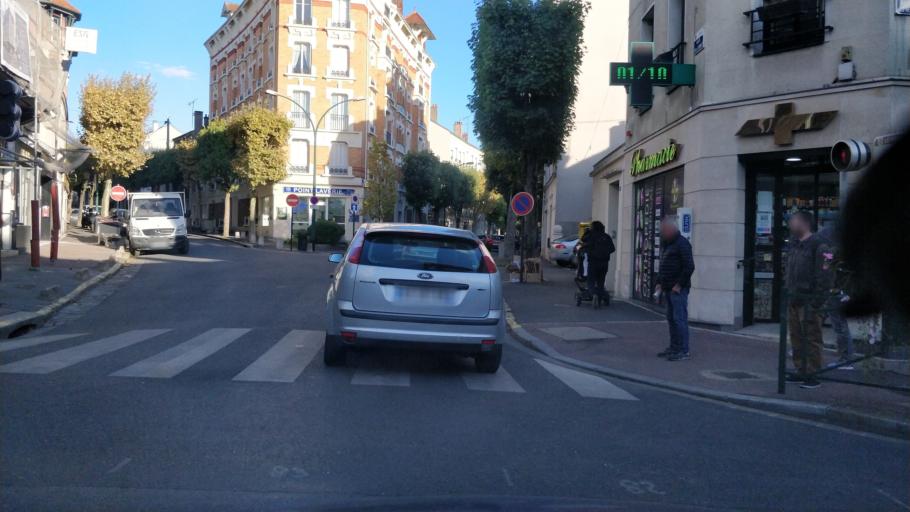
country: FR
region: Ile-de-France
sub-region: Departement de Seine-Saint-Denis
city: Le Raincy
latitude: 48.8926
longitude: 2.5128
